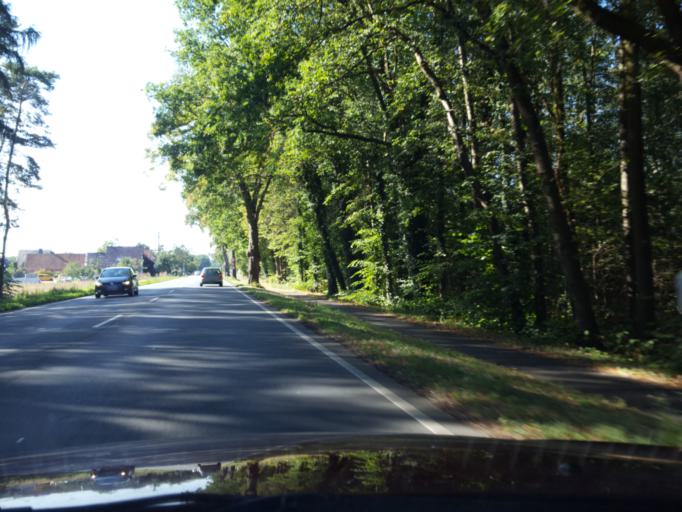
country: DE
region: Lower Saxony
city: Dorverden
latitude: 52.8376
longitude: 9.2163
